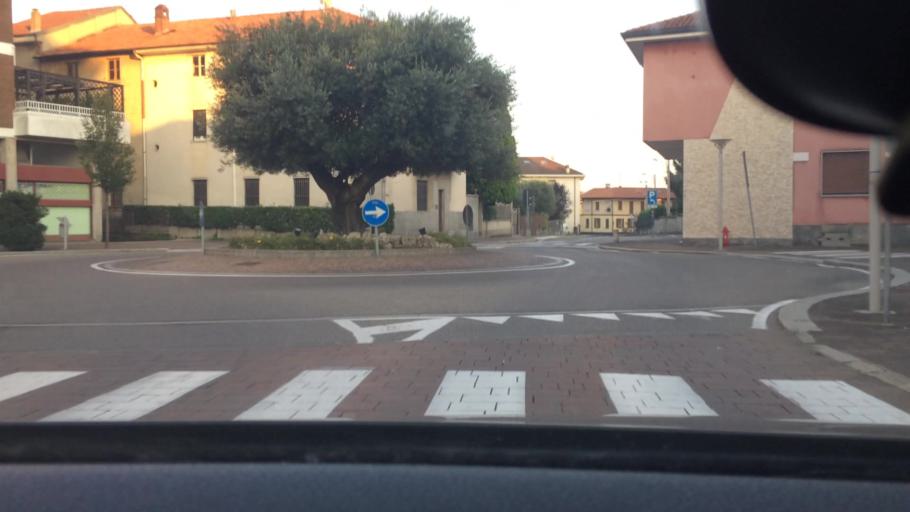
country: IT
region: Lombardy
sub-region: Provincia di Como
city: Rovello Porro
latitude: 45.6541
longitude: 9.0410
